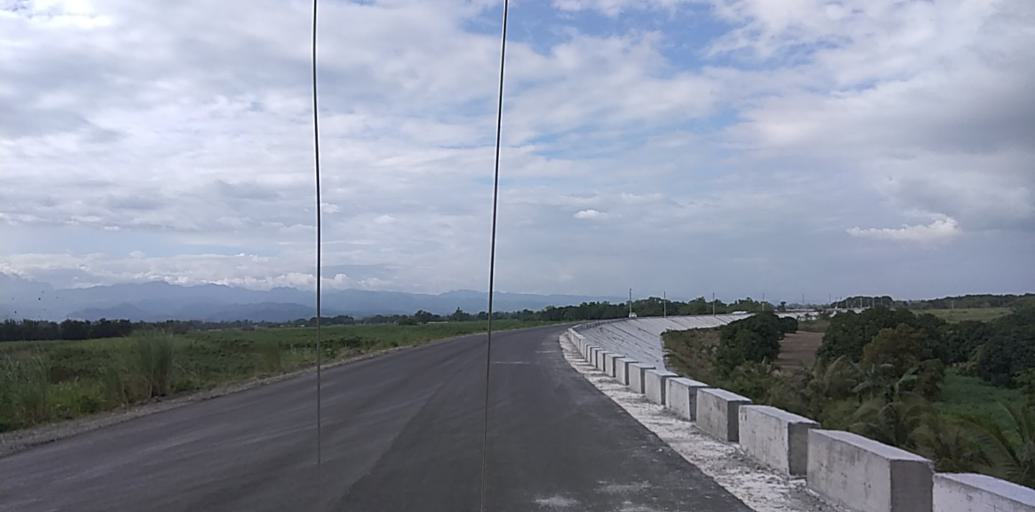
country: PH
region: Central Luzon
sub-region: Province of Pampanga
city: Pulung Santol
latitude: 15.0620
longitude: 120.5621
